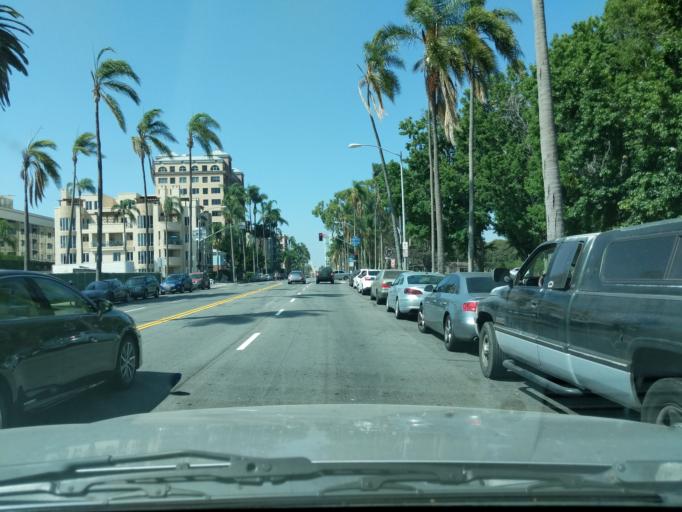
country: US
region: California
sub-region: San Diego County
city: San Diego
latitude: 32.7359
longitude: -117.1594
